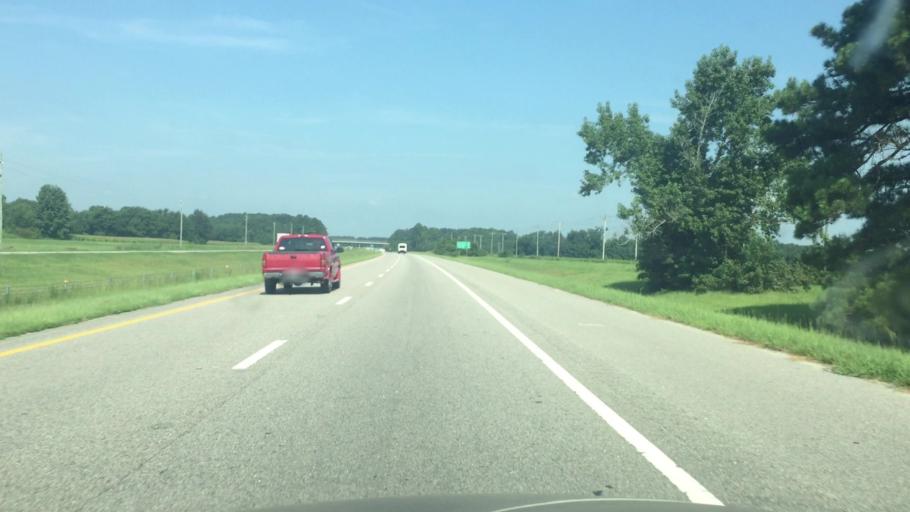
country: US
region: North Carolina
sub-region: Robeson County
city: Lumberton
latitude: 34.5879
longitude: -79.0609
